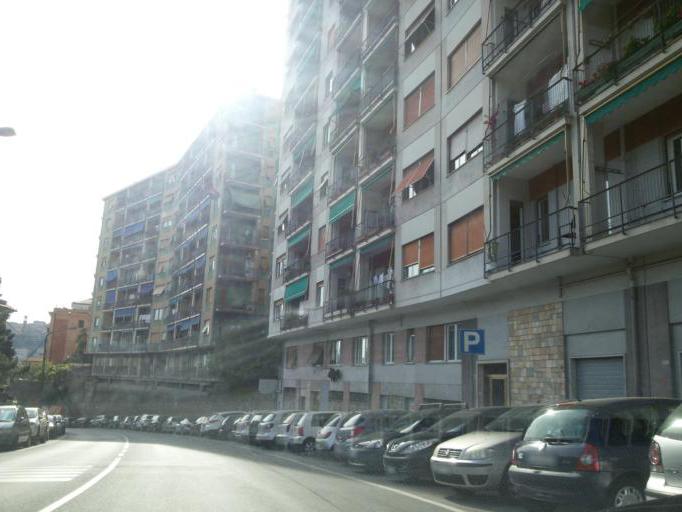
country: IT
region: Liguria
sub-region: Provincia di Genova
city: Genoa
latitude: 44.4183
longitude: 8.9607
